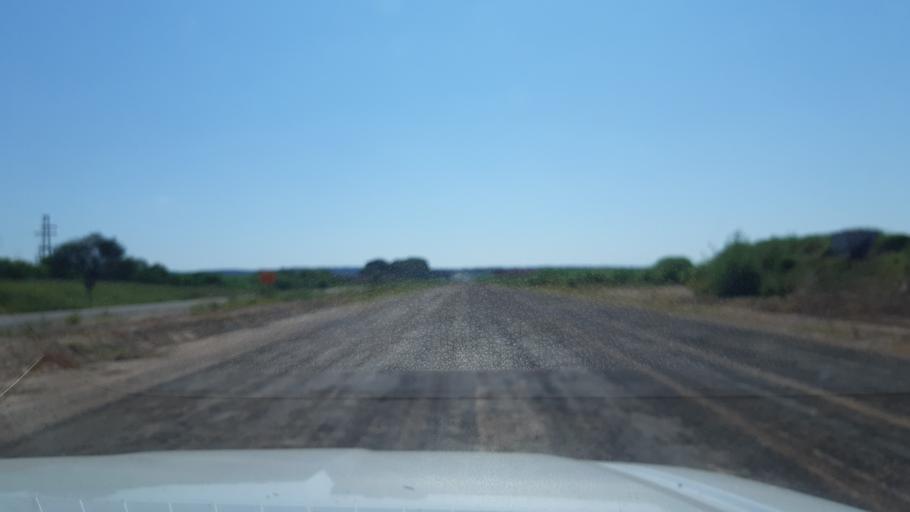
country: AR
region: Jujuy
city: La Mendieta
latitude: -24.3958
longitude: -64.9877
